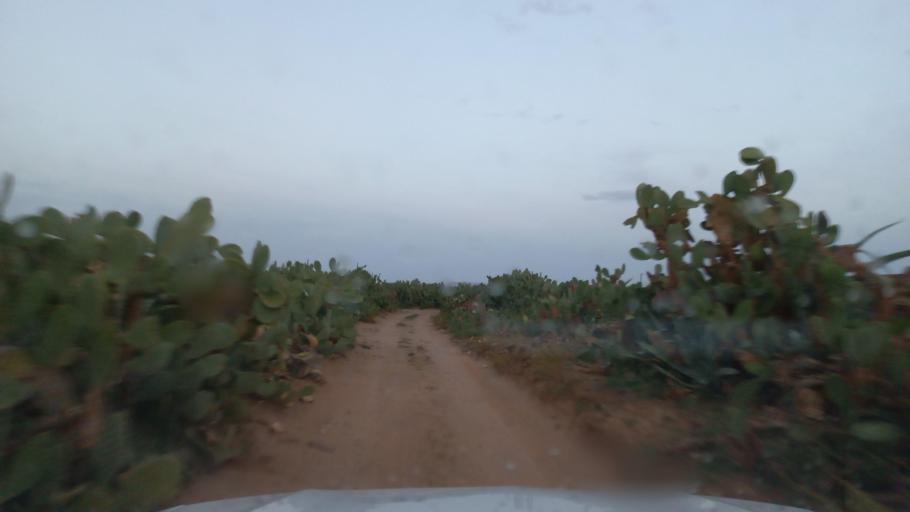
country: TN
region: Al Qasrayn
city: Sbiba
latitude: 35.3537
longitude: 9.0459
